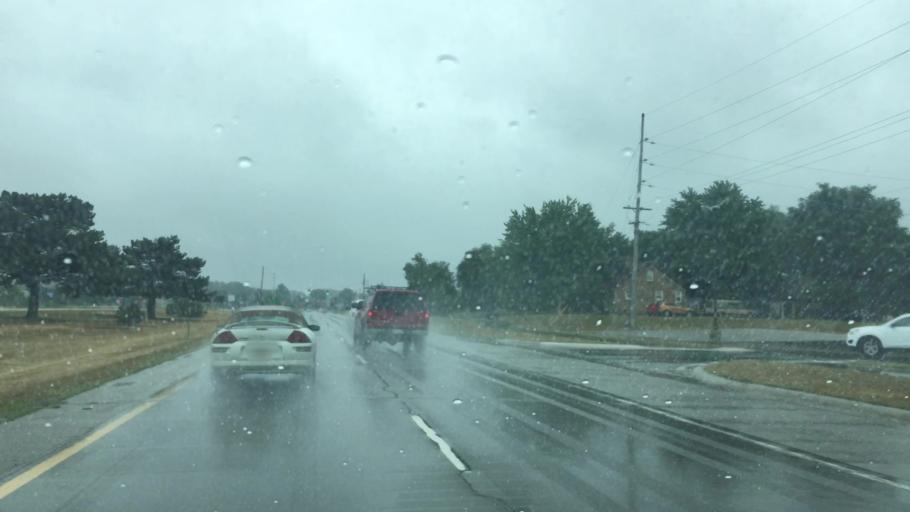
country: US
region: Michigan
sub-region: Ottawa County
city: Jenison
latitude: 42.9013
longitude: -85.7962
